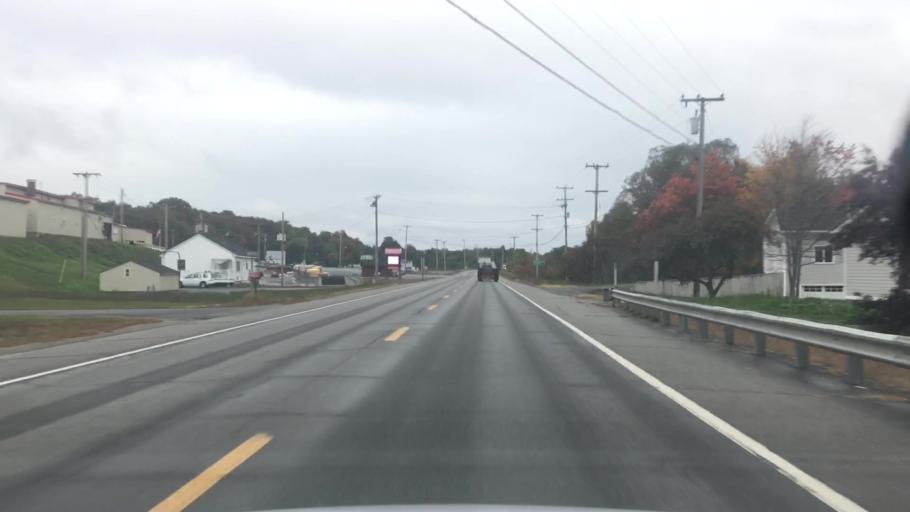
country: US
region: Maine
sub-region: Kennebec County
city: Belgrade
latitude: 44.4448
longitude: -69.8318
